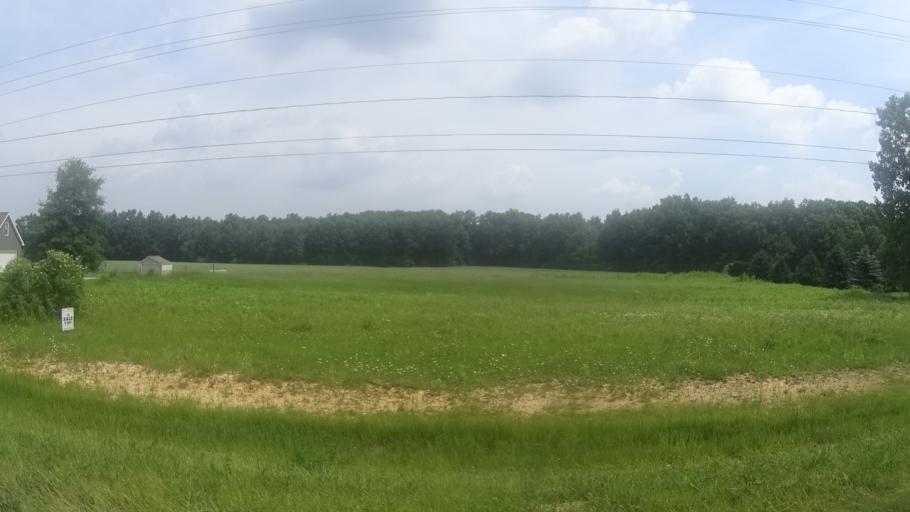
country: US
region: Ohio
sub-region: Erie County
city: Milan
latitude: 41.3421
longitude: -82.6664
